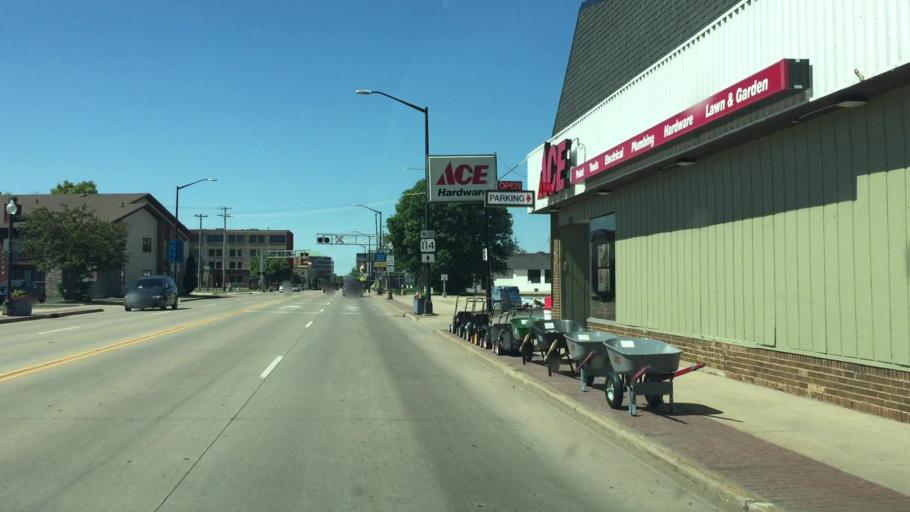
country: US
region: Wisconsin
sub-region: Winnebago County
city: Neenah
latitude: 44.1934
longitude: -88.4553
